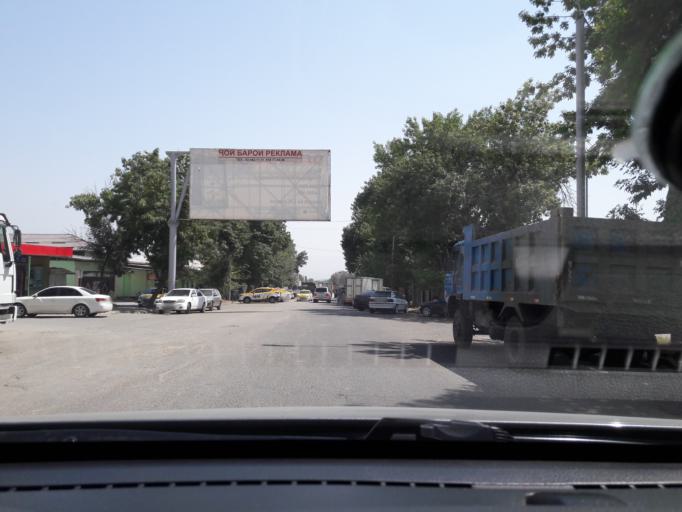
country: TJ
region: Dushanbe
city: Dushanbe
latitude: 38.5871
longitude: 68.7334
